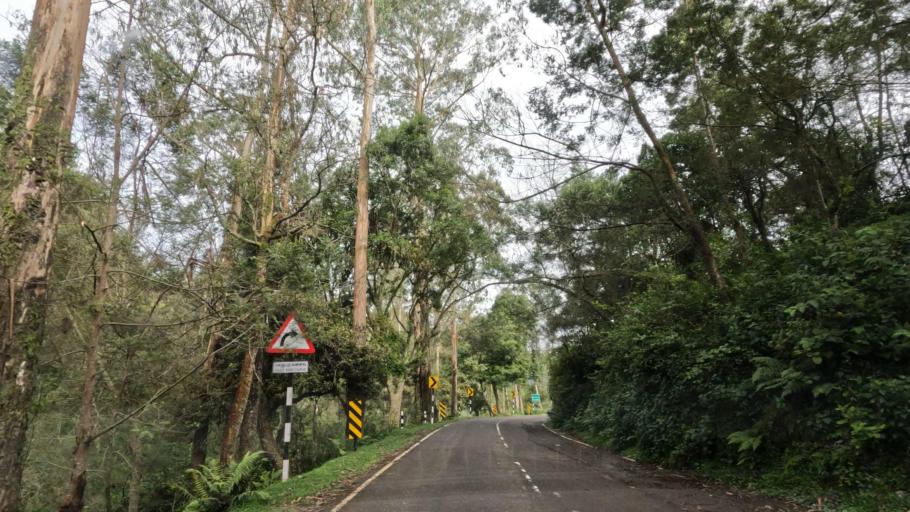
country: IN
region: Tamil Nadu
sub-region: Dindigul
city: Kodaikanal
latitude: 10.2116
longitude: 77.4652
